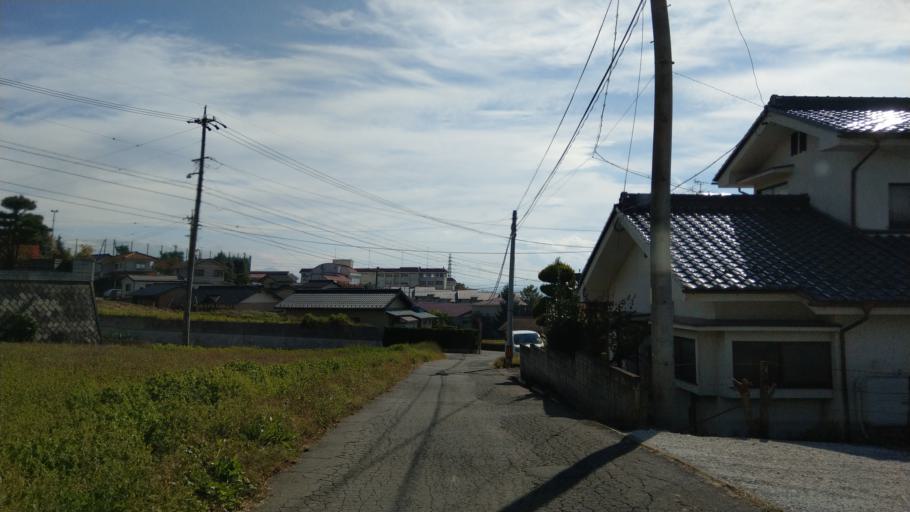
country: JP
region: Nagano
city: Komoro
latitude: 36.3333
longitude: 138.4427
